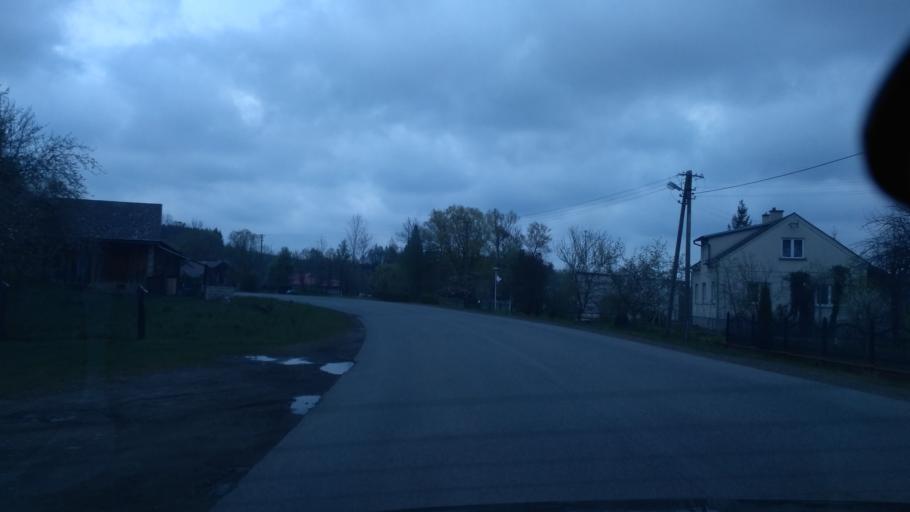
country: PL
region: Subcarpathian Voivodeship
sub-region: Powiat brzozowski
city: Nozdrzec
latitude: 49.7522
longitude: 22.2211
